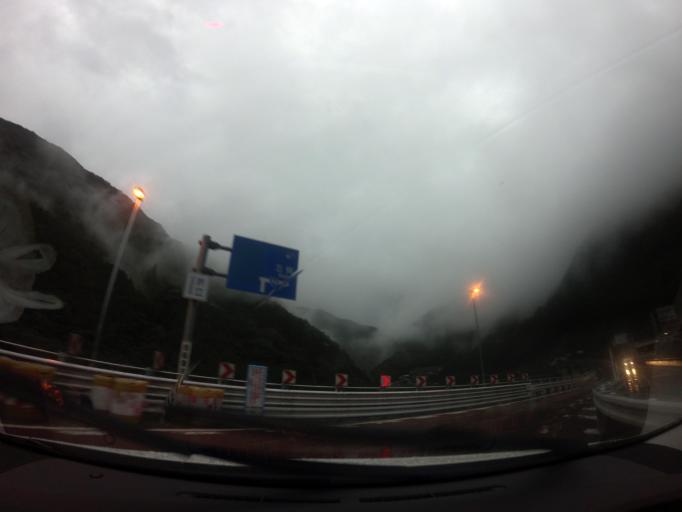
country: JP
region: Wakayama
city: Shingu
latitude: 33.9509
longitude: 135.8003
